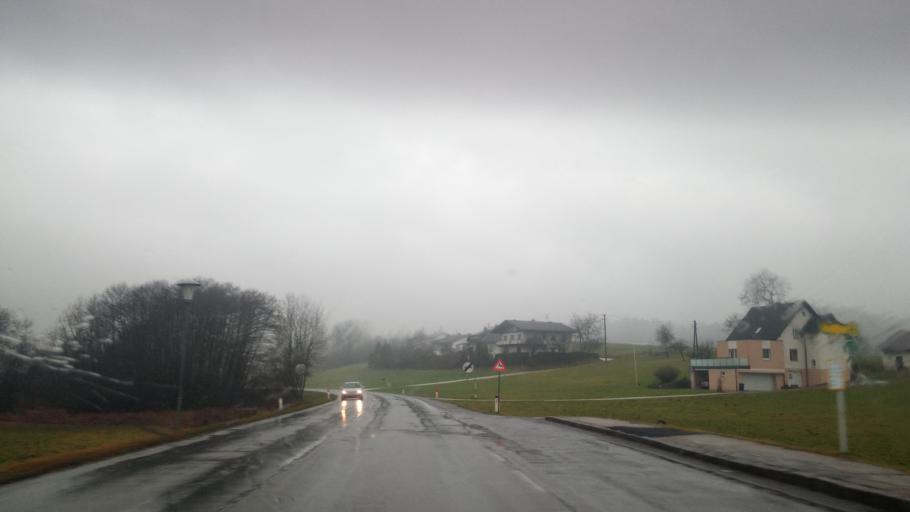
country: AT
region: Carinthia
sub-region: Politischer Bezirk Klagenfurt Land
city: Kottmannsdorf
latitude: 46.5891
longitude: 14.2313
